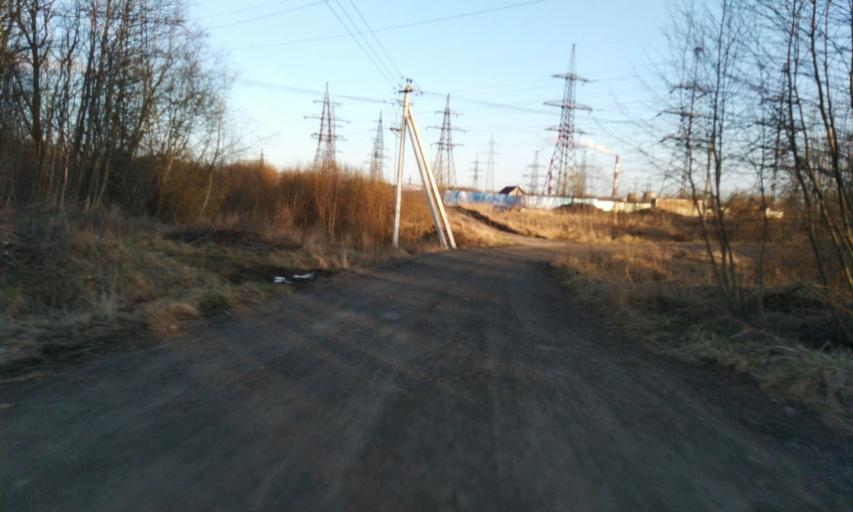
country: RU
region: Leningrad
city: Novoye Devyatkino
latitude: 60.0909
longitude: 30.4594
